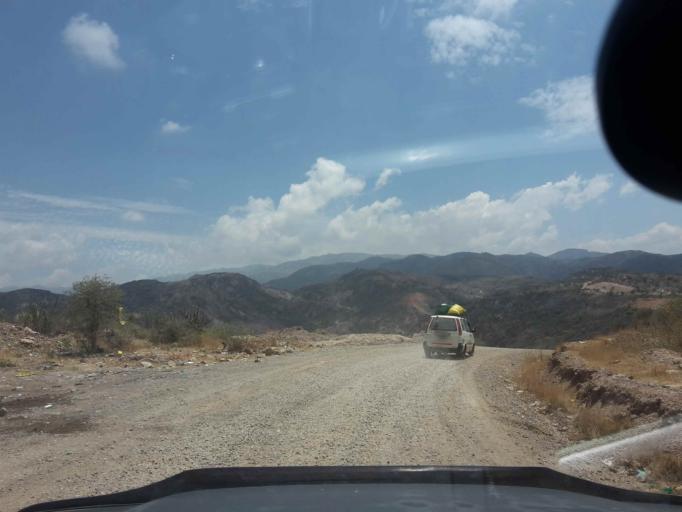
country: BO
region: Cochabamba
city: Sipe Sipe
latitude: -17.5707
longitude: -66.3498
